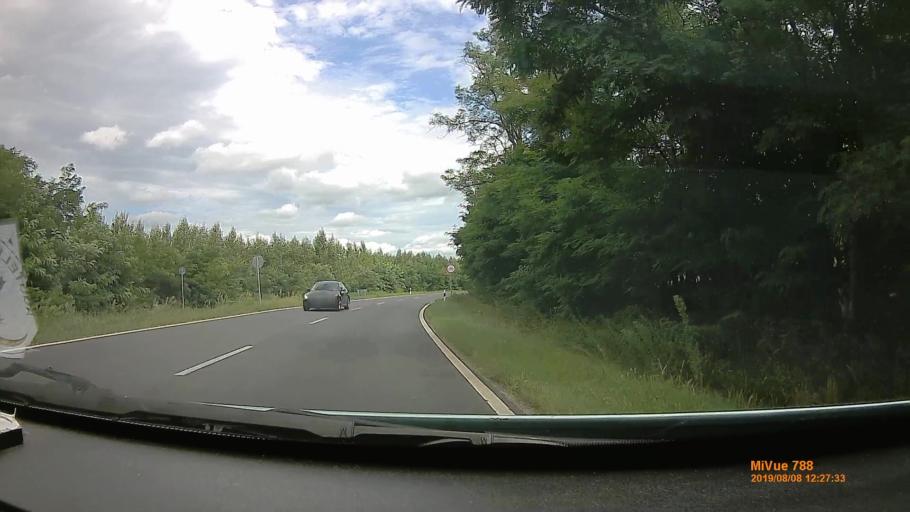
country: HU
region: Szabolcs-Szatmar-Bereg
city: Nyirbator
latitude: 47.8239
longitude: 22.0998
